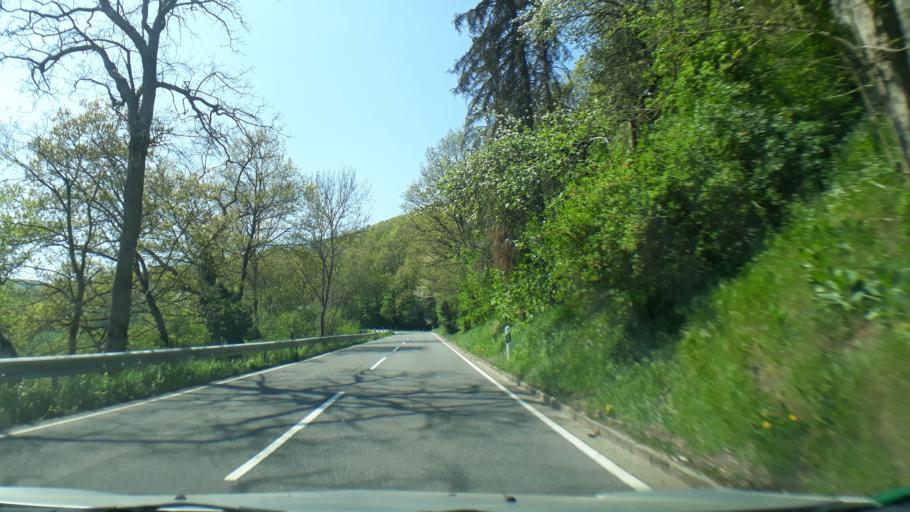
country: DE
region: North Rhine-Westphalia
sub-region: Regierungsbezirk Koln
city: Nideggen
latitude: 50.6871
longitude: 6.4413
